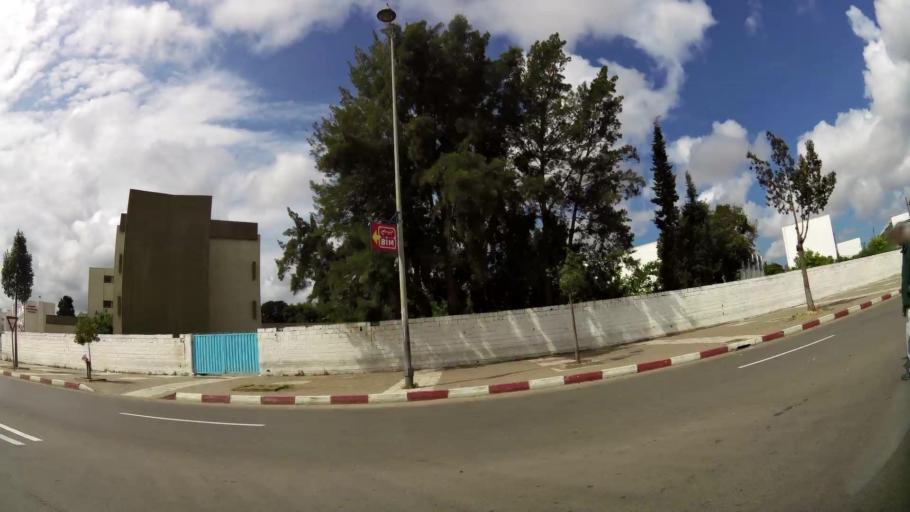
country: MA
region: Gharb-Chrarda-Beni Hssen
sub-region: Kenitra Province
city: Kenitra
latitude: 34.2582
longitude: -6.5634
